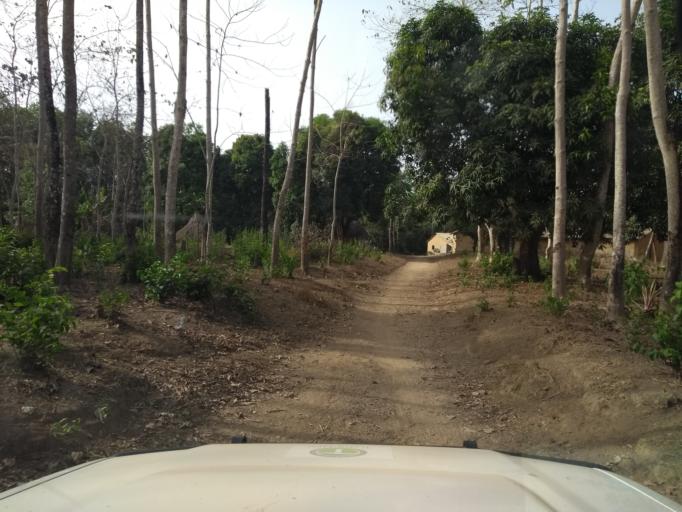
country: GN
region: Kindia
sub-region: Prefecture de Dubreka
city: Dubreka
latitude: 9.8308
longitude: -13.5564
